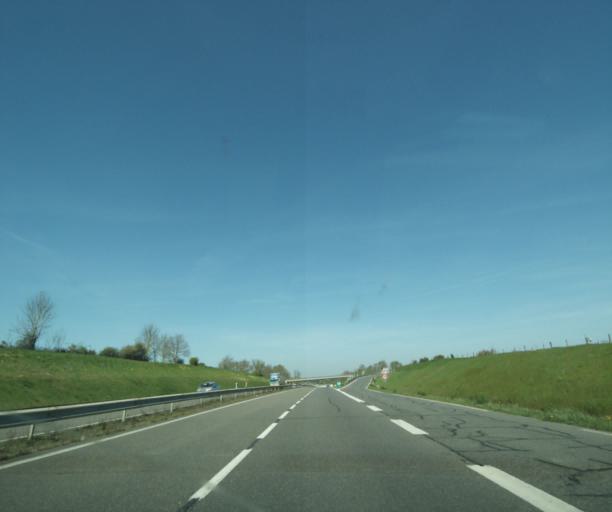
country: FR
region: Bourgogne
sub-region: Departement de la Nievre
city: Saint-Pierre-le-Moutier
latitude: 46.7826
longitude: 3.1281
